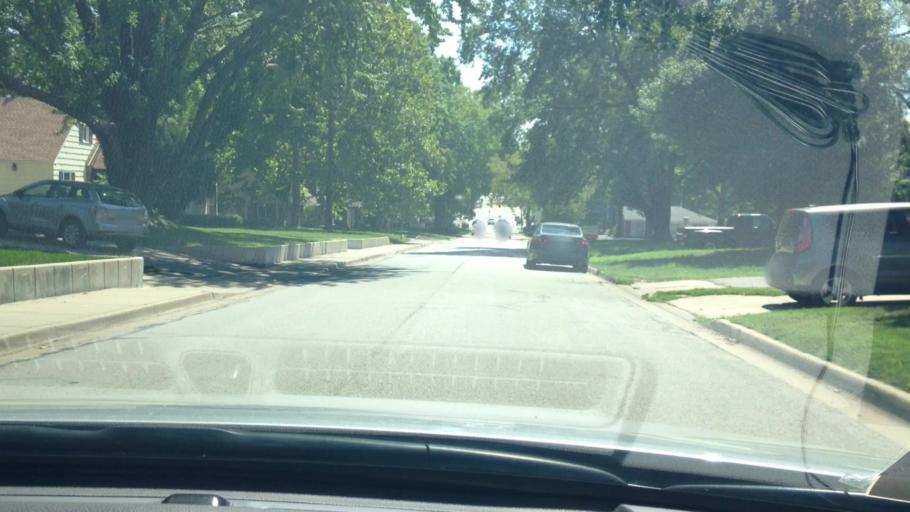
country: US
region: Kansas
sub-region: Johnson County
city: Mission
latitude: 39.0247
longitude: -94.6490
